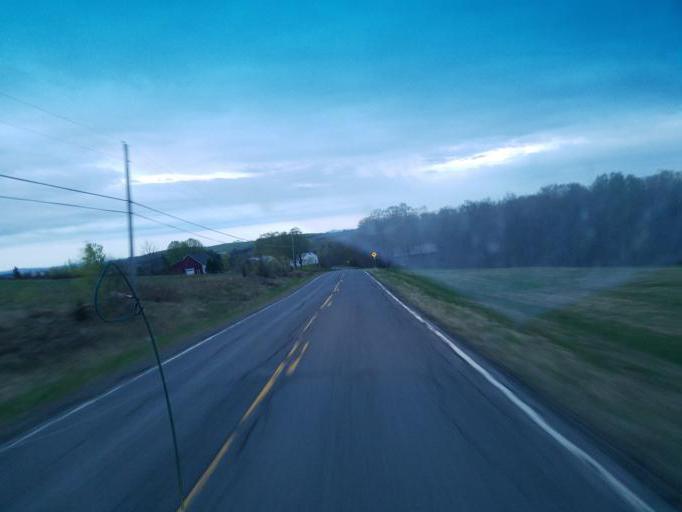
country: US
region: Maine
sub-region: Aroostook County
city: Caribou
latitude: 46.8605
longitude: -68.2086
